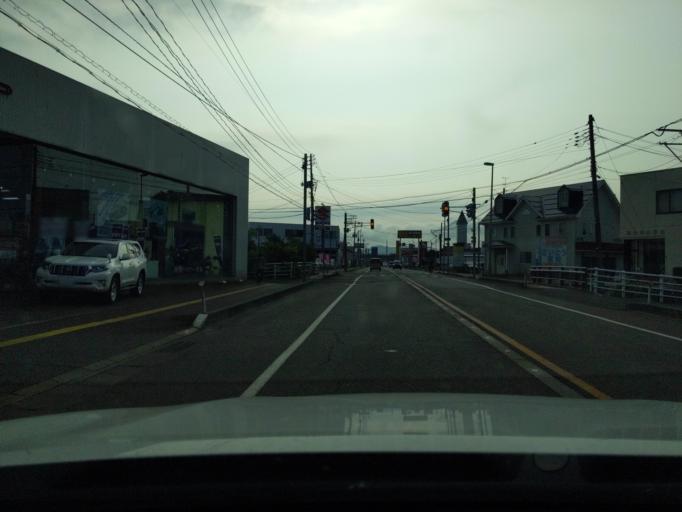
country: JP
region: Niigata
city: Nagaoka
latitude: 37.4508
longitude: 138.8064
